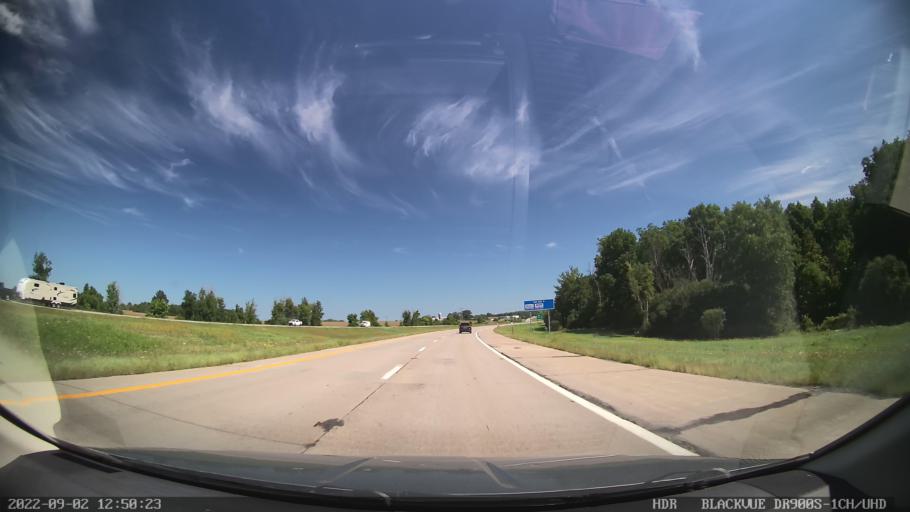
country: US
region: New York
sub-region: Livingston County
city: Avon
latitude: 42.8656
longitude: -77.7235
